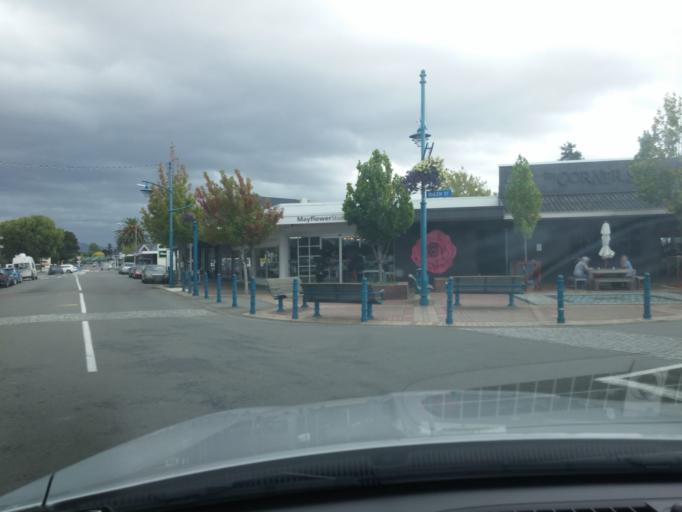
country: NZ
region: Marlborough
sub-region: Marlborough District
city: Blenheim
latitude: -41.5146
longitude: 173.9558
